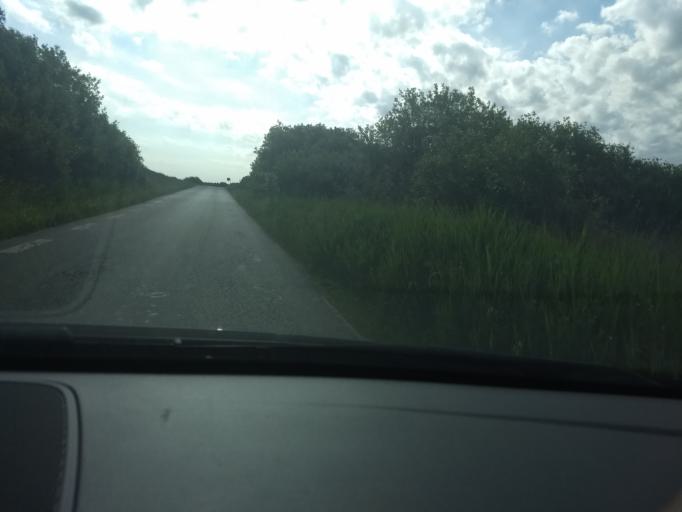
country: DE
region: Schleswig-Holstein
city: List
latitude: 55.1314
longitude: 8.5038
